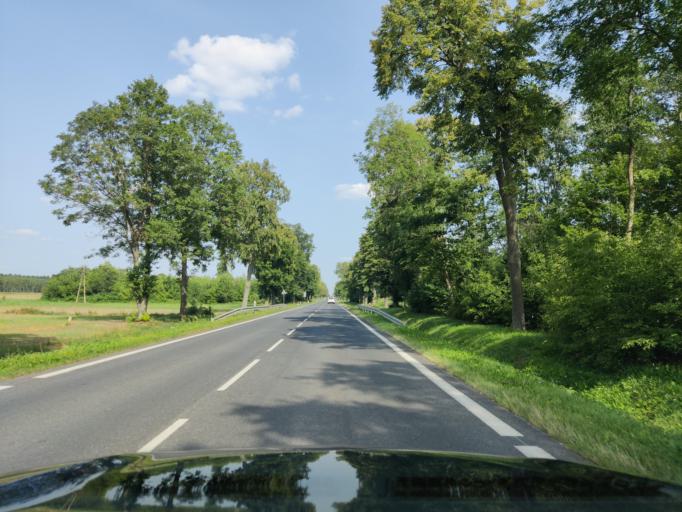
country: PL
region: Masovian Voivodeship
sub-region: Powiat makowski
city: Makow Mazowiecki
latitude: 52.7999
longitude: 21.1441
